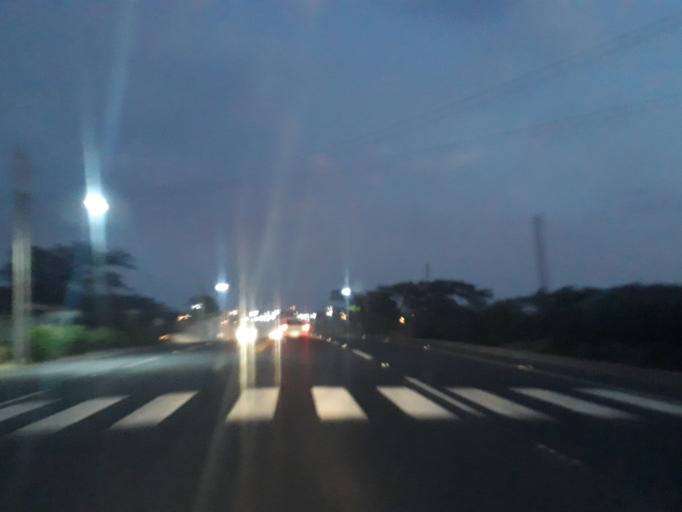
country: NI
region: Managua
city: El Crucero
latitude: 11.9619
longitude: -86.3051
